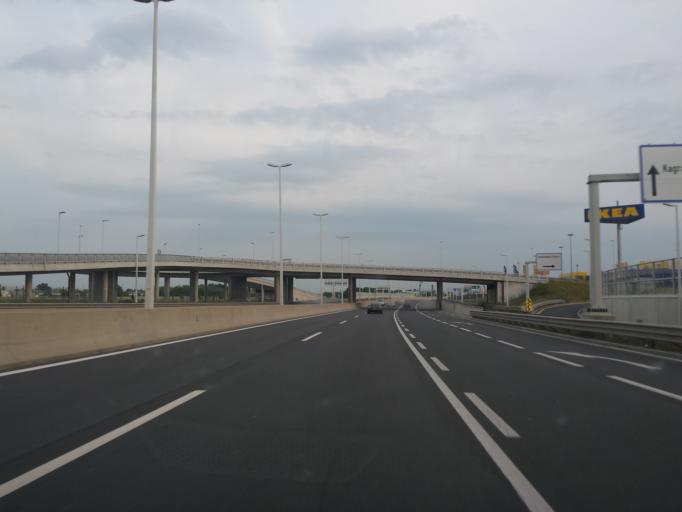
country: AT
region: Lower Austria
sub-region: Politischer Bezirk Wien-Umgebung
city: Gerasdorf bei Wien
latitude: 48.2568
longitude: 16.4746
